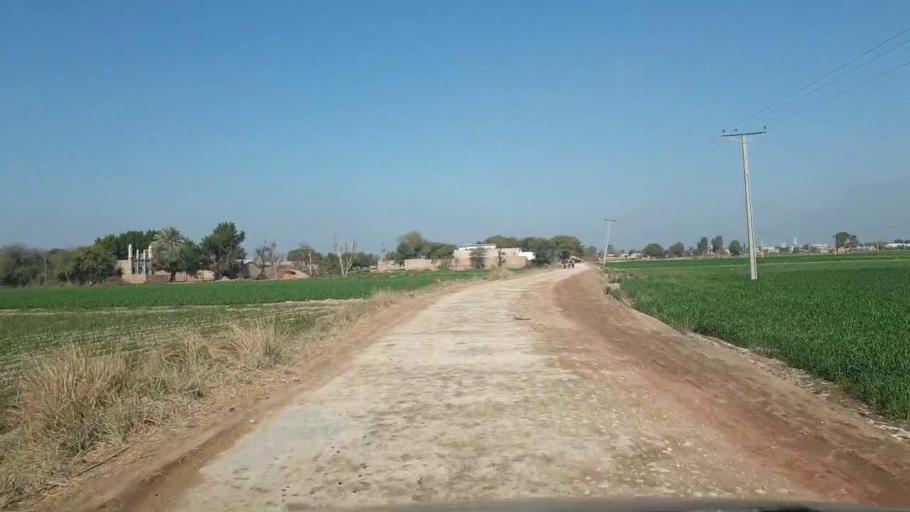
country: PK
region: Sindh
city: Bhit Shah
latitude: 25.8884
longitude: 68.5265
